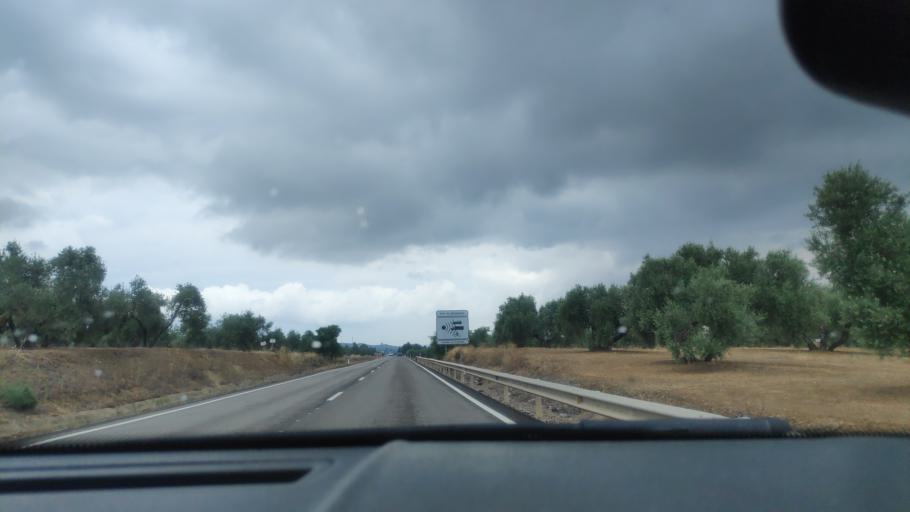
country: ES
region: Andalusia
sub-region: Provincia de Jaen
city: Jabalquinto
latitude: 38.0325
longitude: -3.7618
